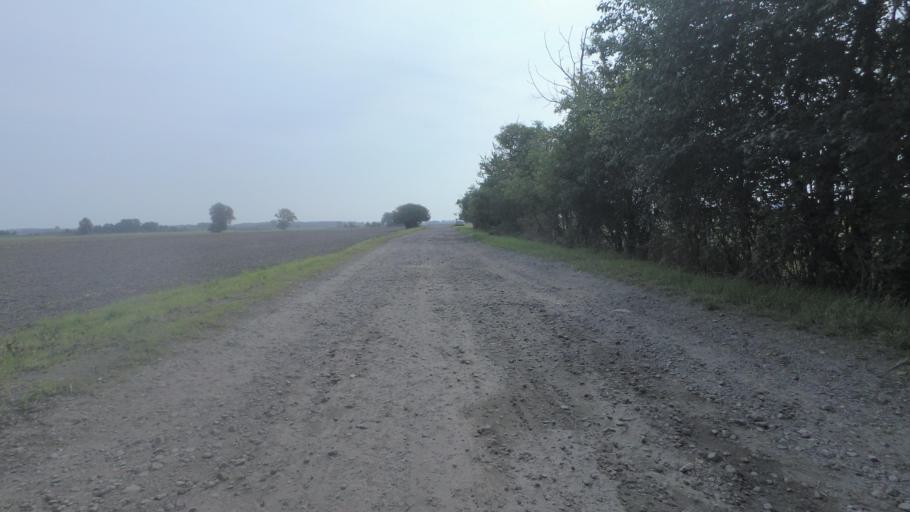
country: DE
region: Brandenburg
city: Rangsdorf
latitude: 52.2813
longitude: 13.3813
